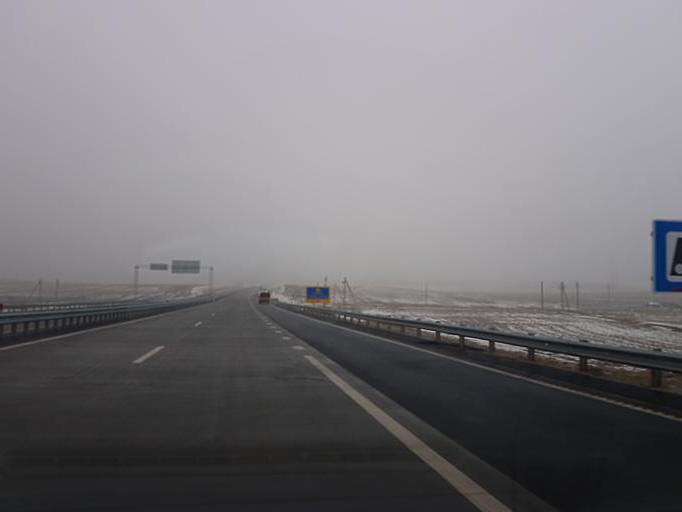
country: BY
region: Minsk
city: Samakhvalavichy
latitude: 53.7072
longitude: 27.4427
